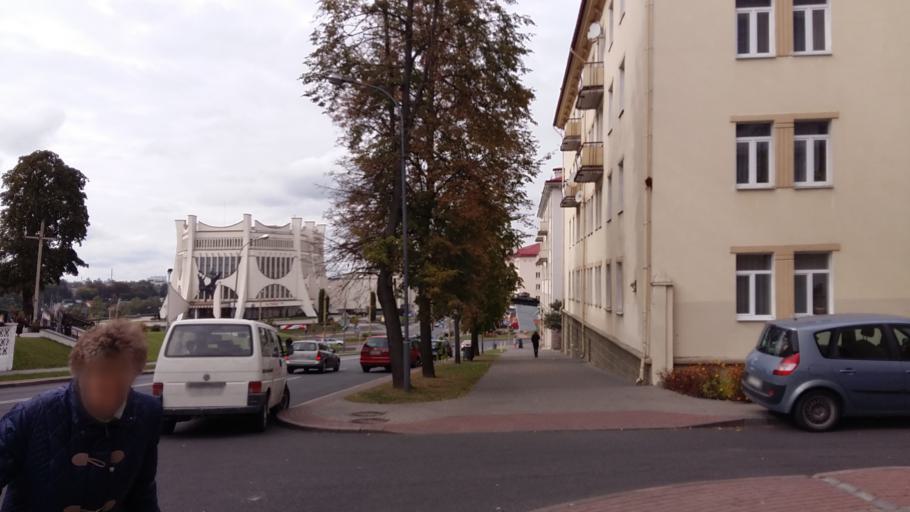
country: BY
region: Grodnenskaya
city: Hrodna
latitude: 53.6753
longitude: 23.8310
